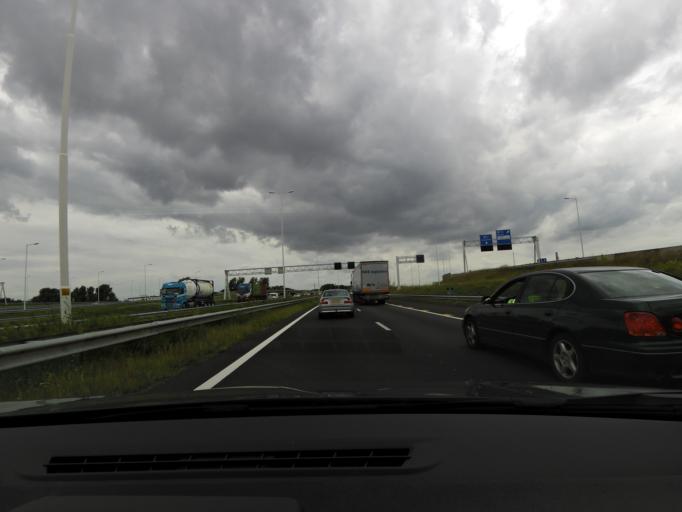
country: NL
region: South Holland
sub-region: Gemeente Albrandswaard
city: Rhoon
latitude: 51.8733
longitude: 4.3843
